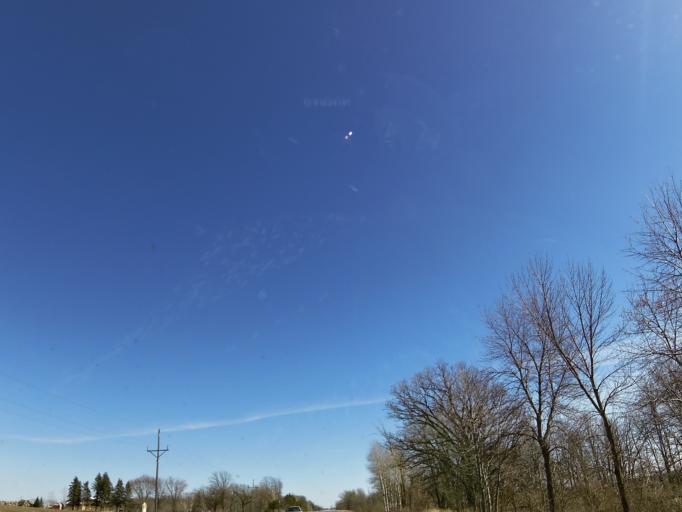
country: US
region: Minnesota
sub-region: Wright County
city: Maple Lake
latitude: 45.2394
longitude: -94.0499
